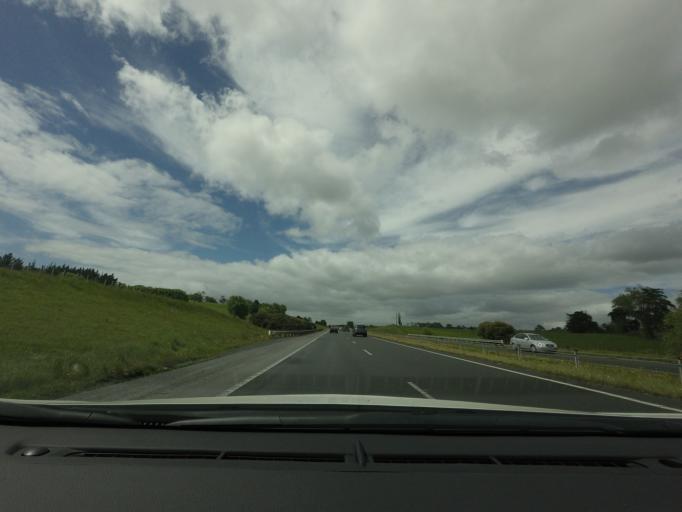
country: NZ
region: Auckland
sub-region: Auckland
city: Rothesay Bay
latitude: -36.6392
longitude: 174.6628
